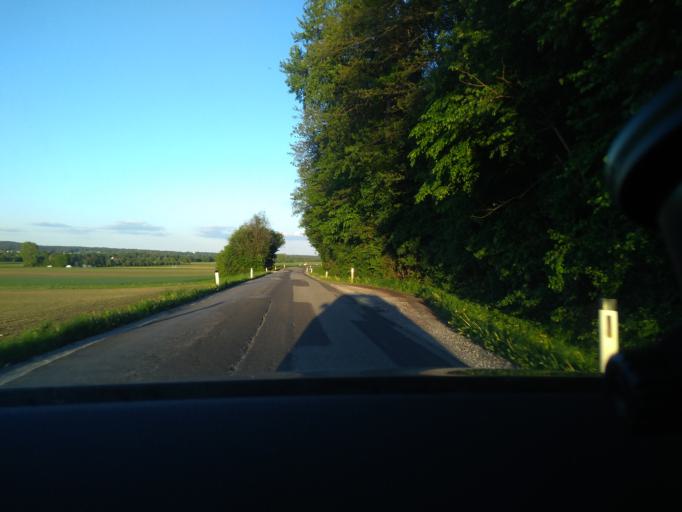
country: AT
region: Styria
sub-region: Politischer Bezirk Voitsberg
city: Mooskirchen
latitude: 46.9738
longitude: 15.2880
